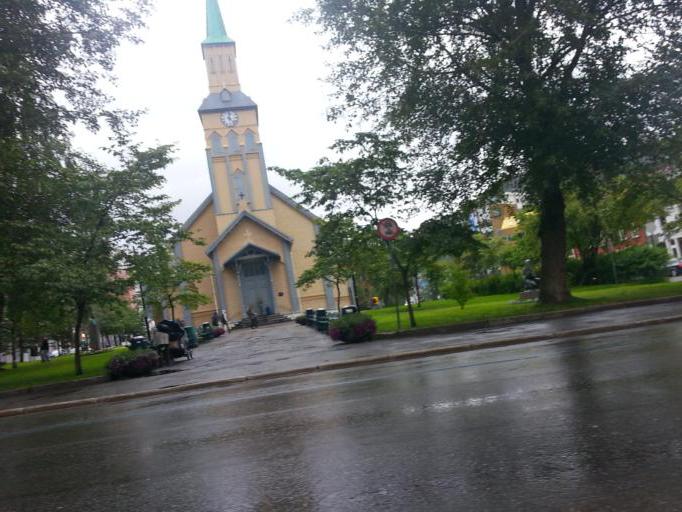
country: NO
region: Troms
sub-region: Tromso
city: Tromso
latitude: 69.6489
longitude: 18.9550
